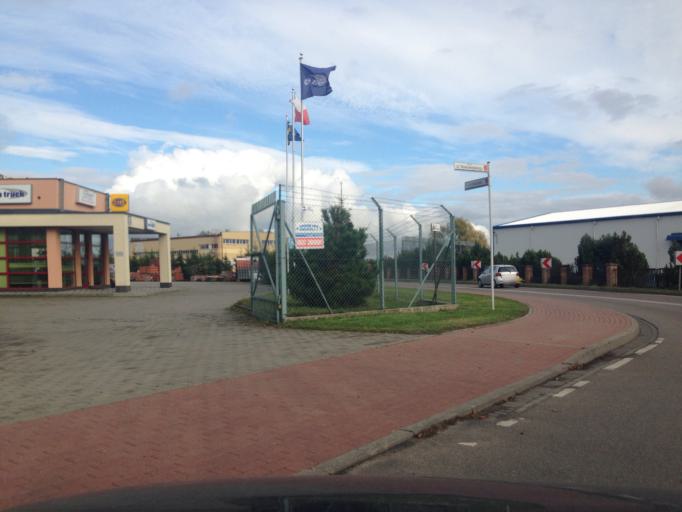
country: PL
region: Pomeranian Voivodeship
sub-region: Powiat gdanski
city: Pruszcz Gdanski
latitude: 54.2507
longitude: 18.6444
